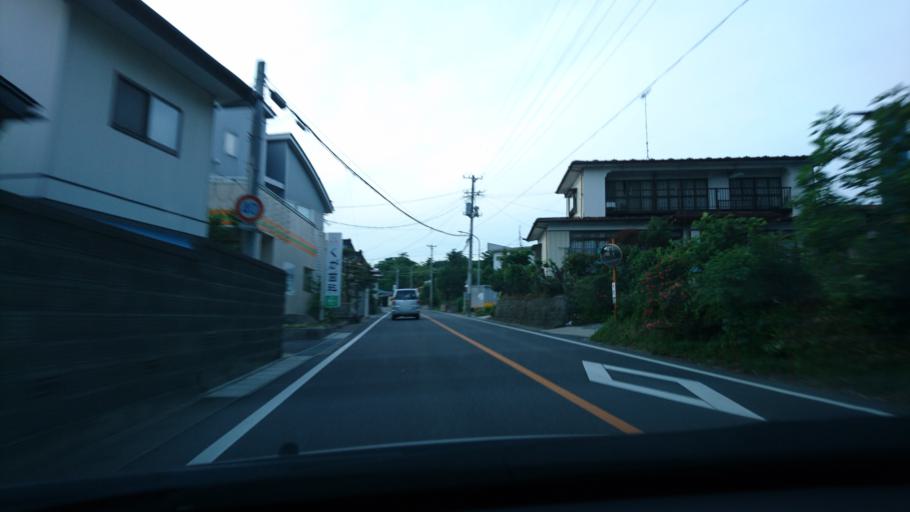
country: JP
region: Miyagi
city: Furukawa
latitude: 38.7516
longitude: 141.0130
